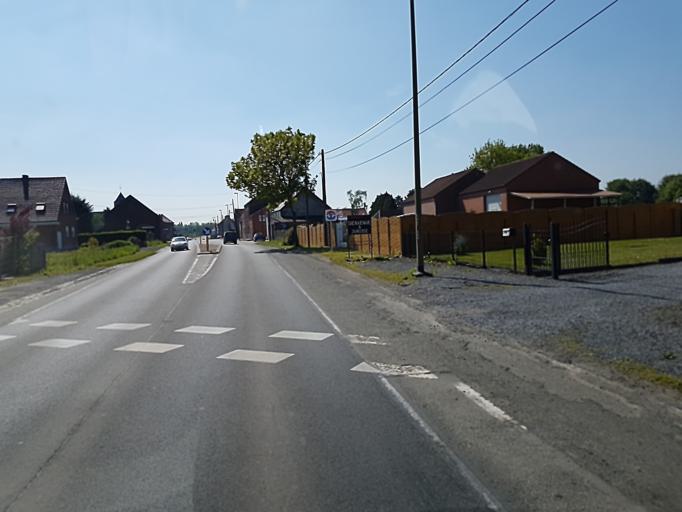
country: BE
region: Wallonia
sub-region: Province du Hainaut
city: Jurbise
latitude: 50.5358
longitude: 3.9096
